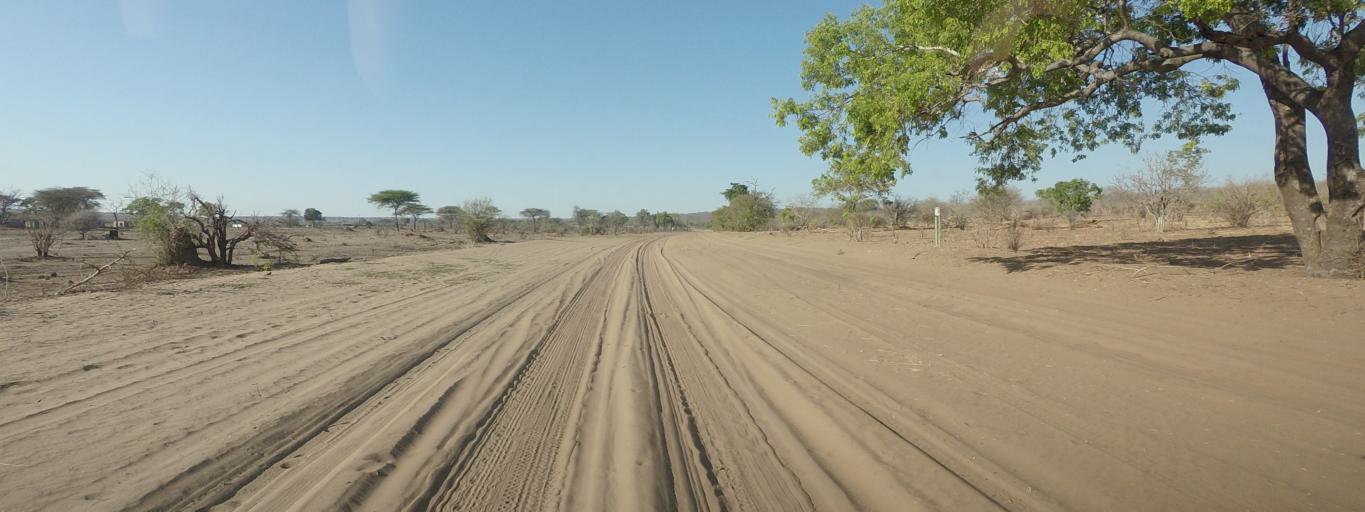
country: BW
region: North West
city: Kasane
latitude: -17.8811
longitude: 25.2337
